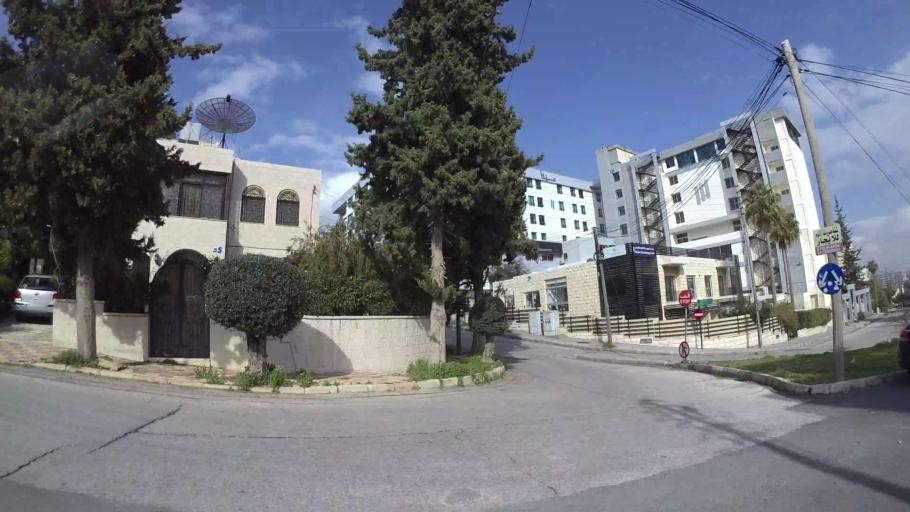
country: JO
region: Amman
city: Amman
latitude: 31.9626
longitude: 35.8910
